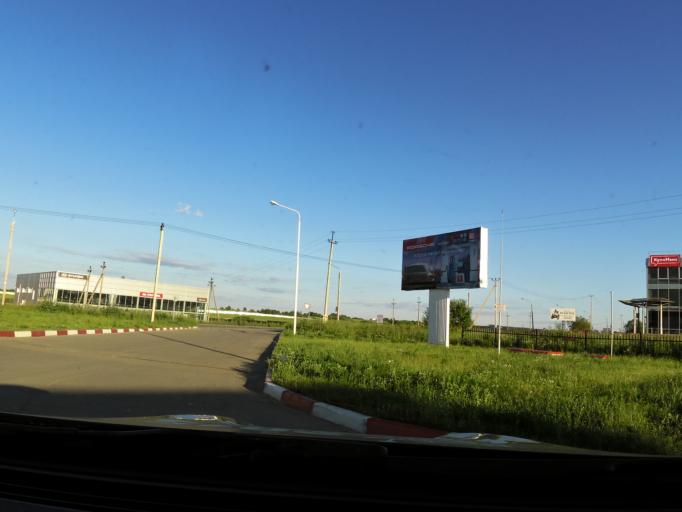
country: RU
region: Vologda
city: Vologda
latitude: 59.1837
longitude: 39.8963
